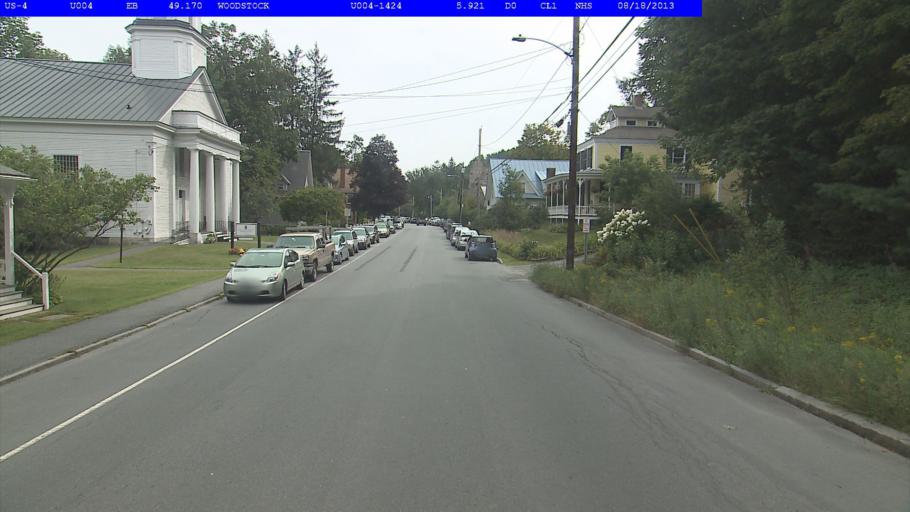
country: US
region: Vermont
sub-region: Windsor County
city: Woodstock
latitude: 43.6222
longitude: -72.5235
